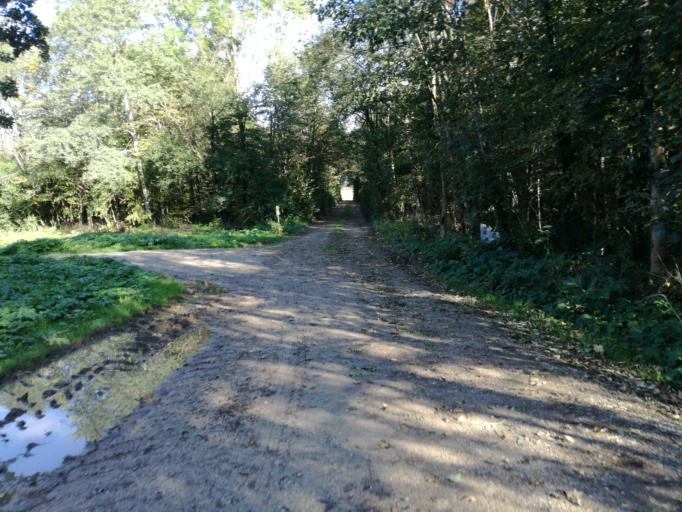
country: DE
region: Bavaria
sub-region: Upper Bavaria
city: Planegg
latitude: 48.0937
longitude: 11.4309
